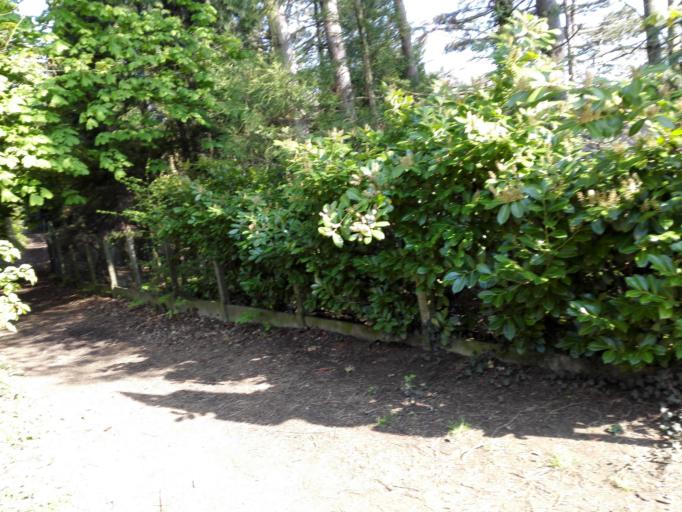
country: BE
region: Flanders
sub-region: Provincie Vlaams-Brabant
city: Leuven
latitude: 50.8724
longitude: 4.7382
